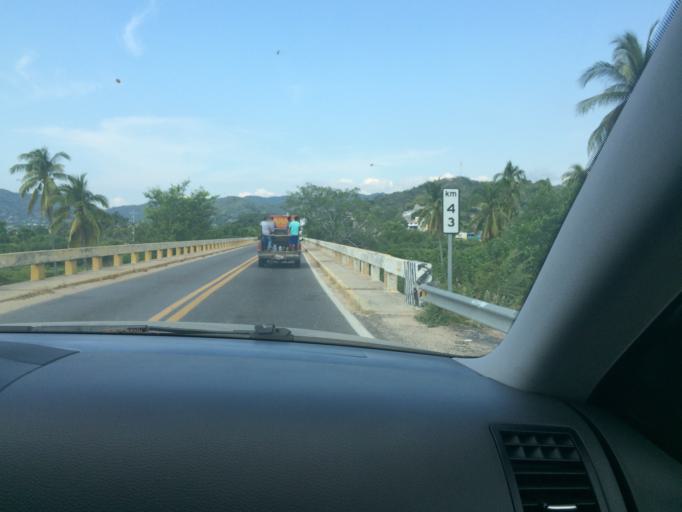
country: MX
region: Jalisco
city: Cihuatlan
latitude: 19.2353
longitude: -104.5520
